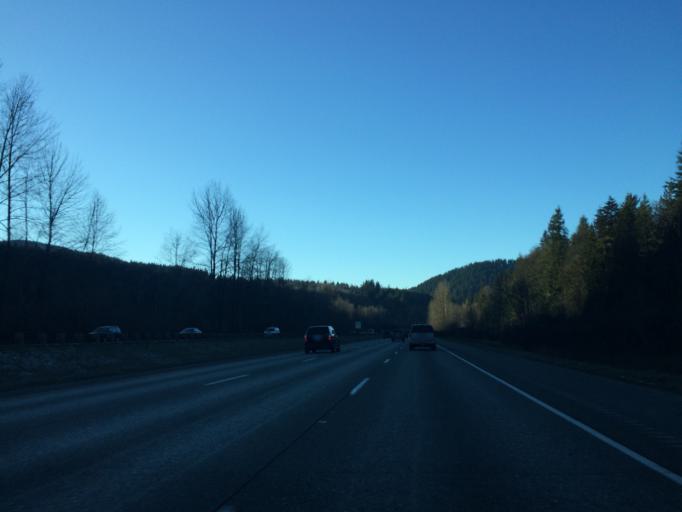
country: US
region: Washington
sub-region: King County
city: Fall City
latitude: 47.5322
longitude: -121.9486
